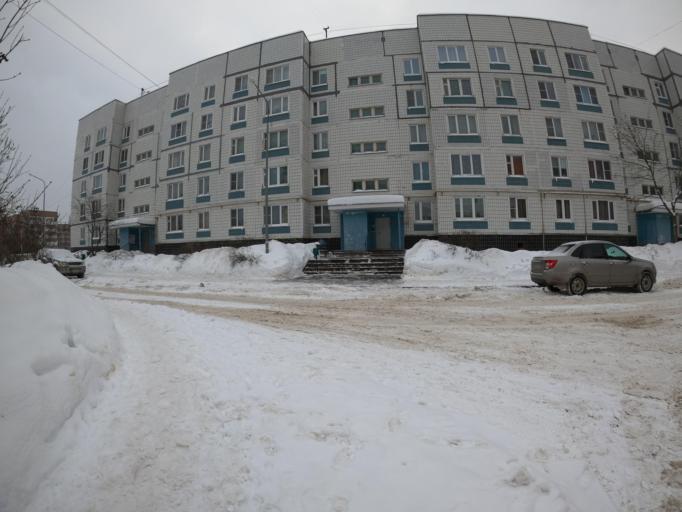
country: RU
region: Moskovskaya
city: Elektrogorsk
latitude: 55.8731
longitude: 38.7774
